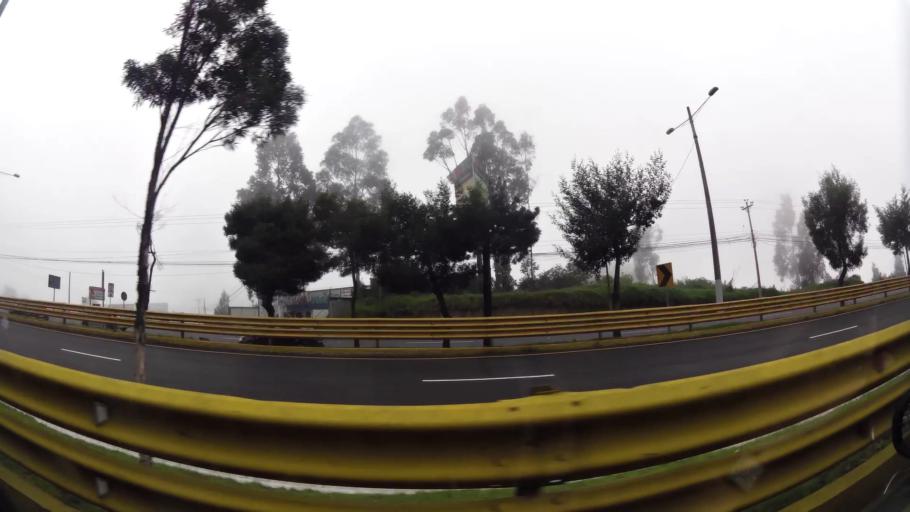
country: EC
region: Pichincha
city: Quito
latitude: -0.2577
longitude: -78.4856
